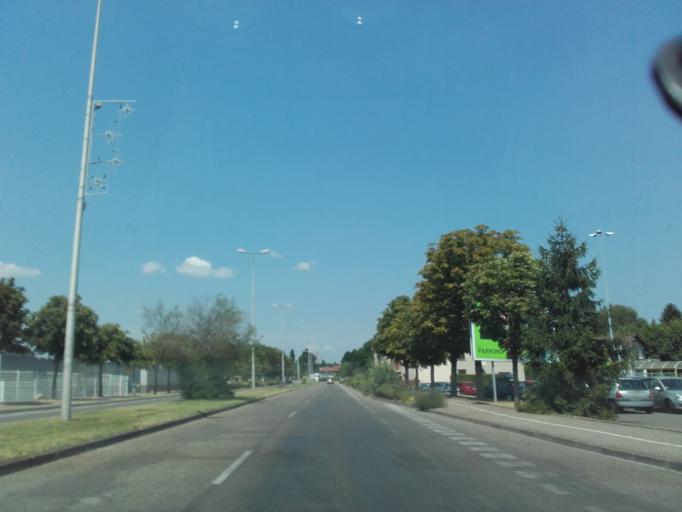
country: FR
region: Rhone-Alpes
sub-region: Departement de l'Isere
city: Bourgoin-Jallieu
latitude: 45.5965
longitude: 5.2686
